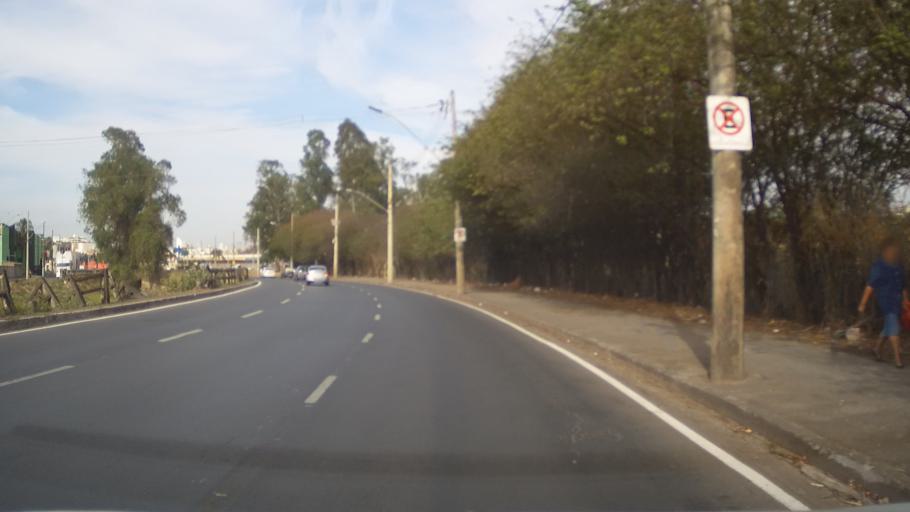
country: BR
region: Minas Gerais
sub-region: Contagem
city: Contagem
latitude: -19.8730
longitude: -44.0238
